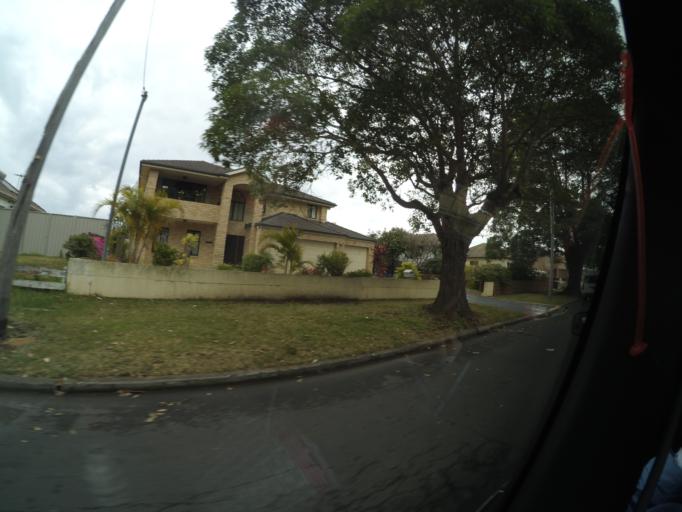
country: AU
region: New South Wales
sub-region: Bankstown
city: Bankstown
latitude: -33.9085
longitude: 151.0203
